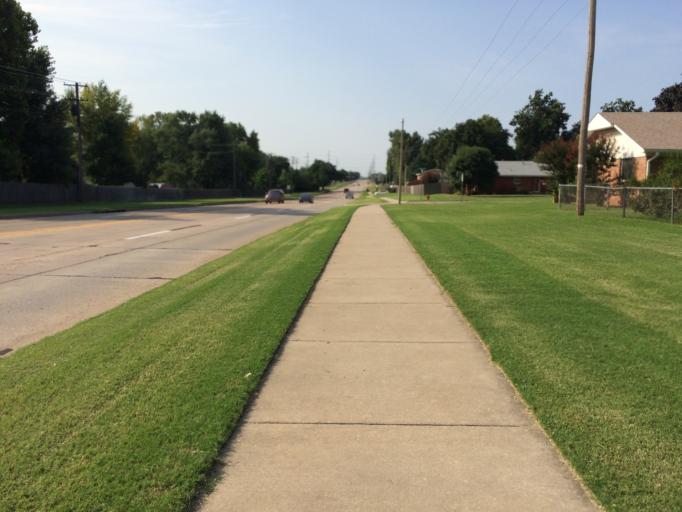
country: US
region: Oklahoma
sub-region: Cleveland County
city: Norman
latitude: 35.2159
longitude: -97.4768
